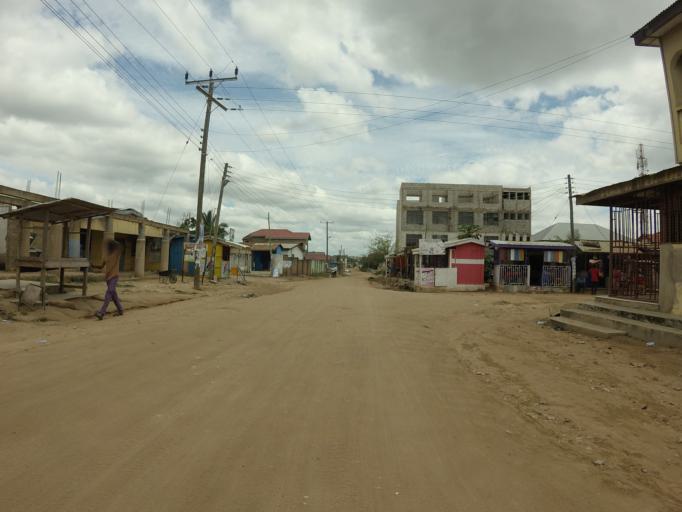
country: GH
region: Central
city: Kasoa
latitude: 5.5475
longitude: -0.3976
